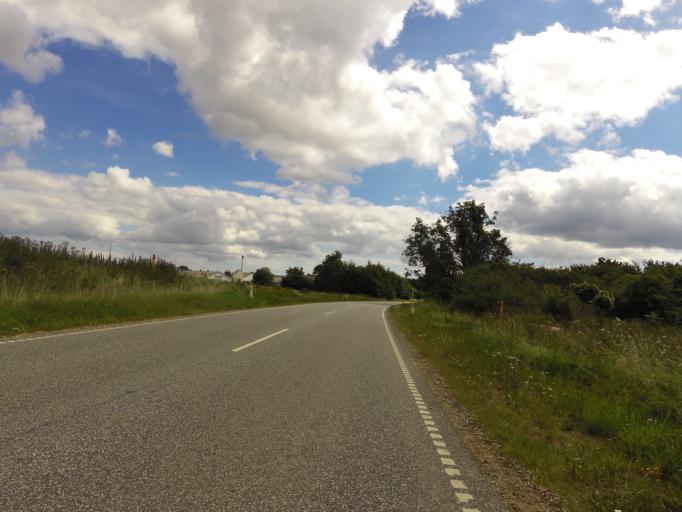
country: DK
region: South Denmark
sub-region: Haderslev Kommune
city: Haderslev
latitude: 55.2767
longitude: 9.4192
